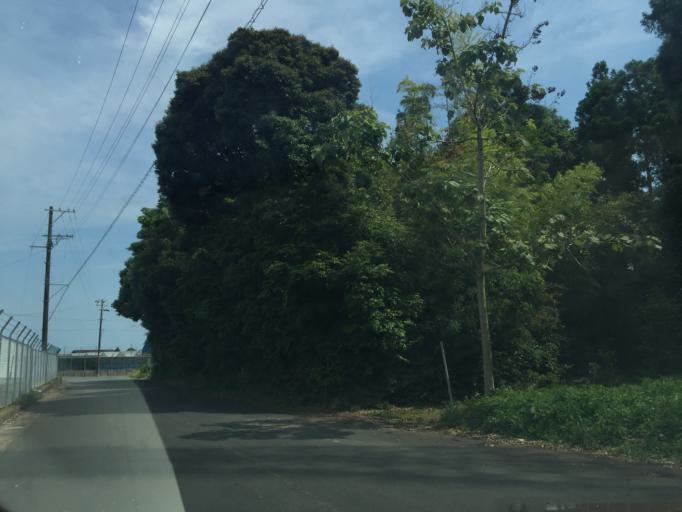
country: JP
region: Shizuoka
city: Mori
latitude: 34.7983
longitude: 137.9406
